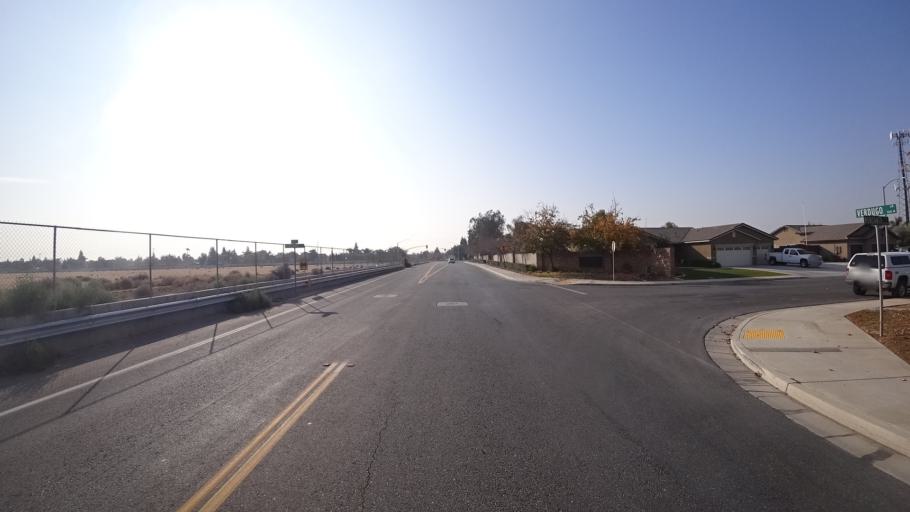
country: US
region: California
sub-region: Kern County
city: Greenacres
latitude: 35.4286
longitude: -119.1191
